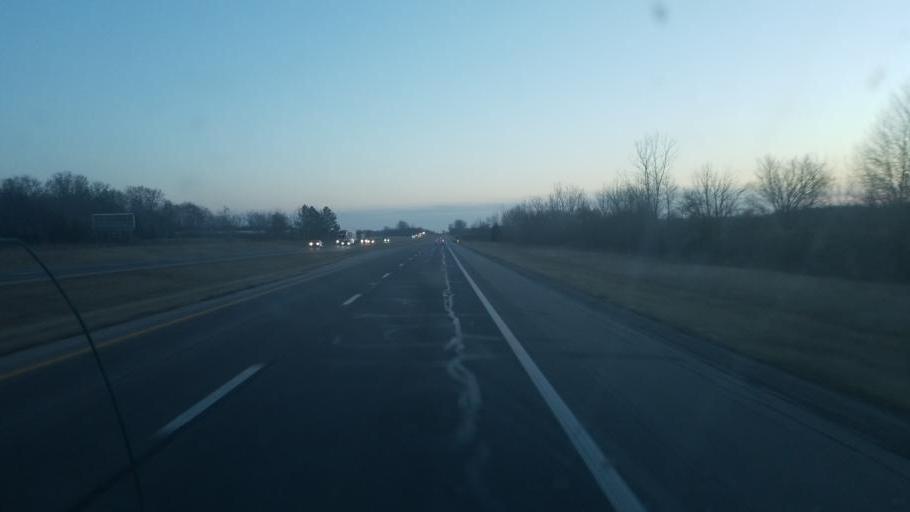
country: US
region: Ohio
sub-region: Marion County
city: Marion
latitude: 40.5579
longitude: -83.0745
